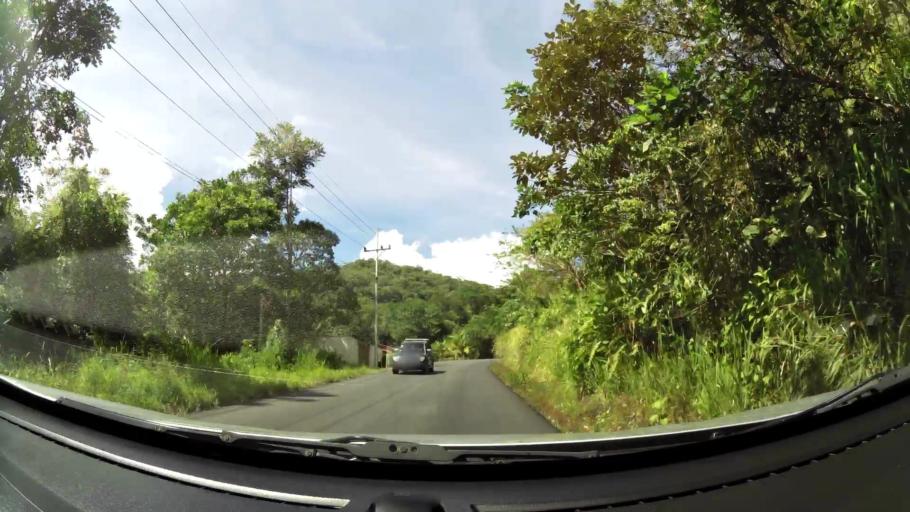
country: CR
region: San Jose
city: San Isidro
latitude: 9.3307
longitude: -83.7374
